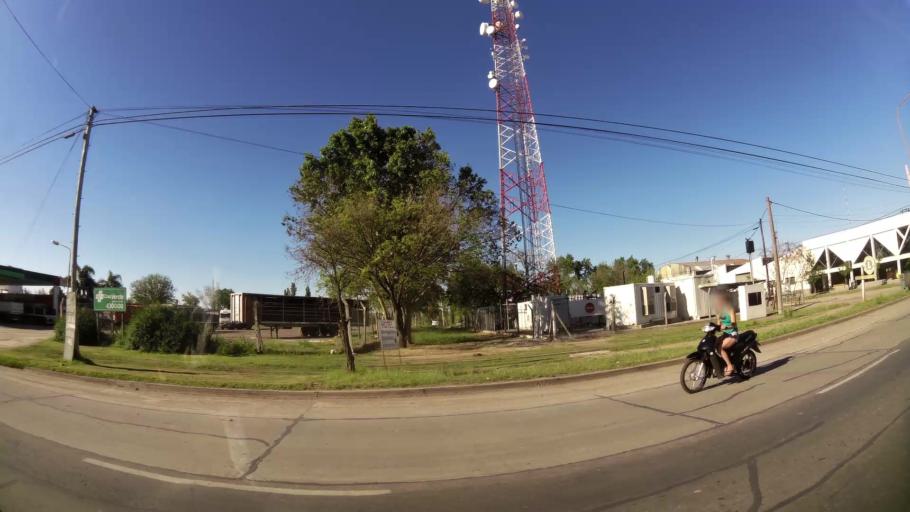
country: AR
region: Cordoba
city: San Francisco
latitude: -31.4179
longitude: -62.0758
